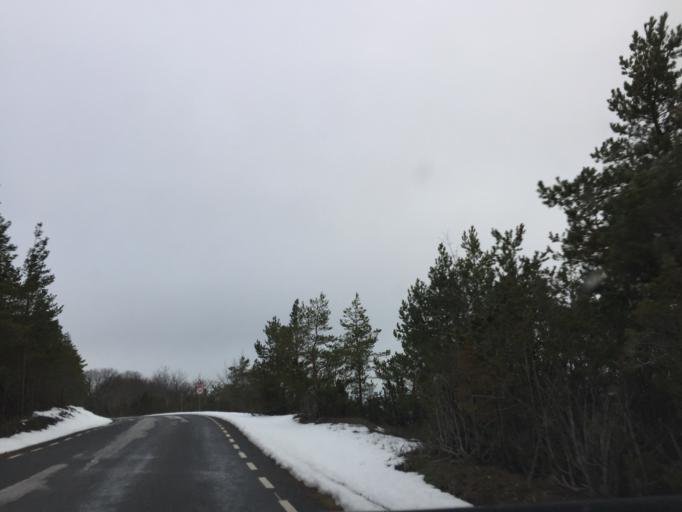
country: EE
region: Saare
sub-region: Kuressaare linn
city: Kuressaare
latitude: 58.5665
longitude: 22.3063
